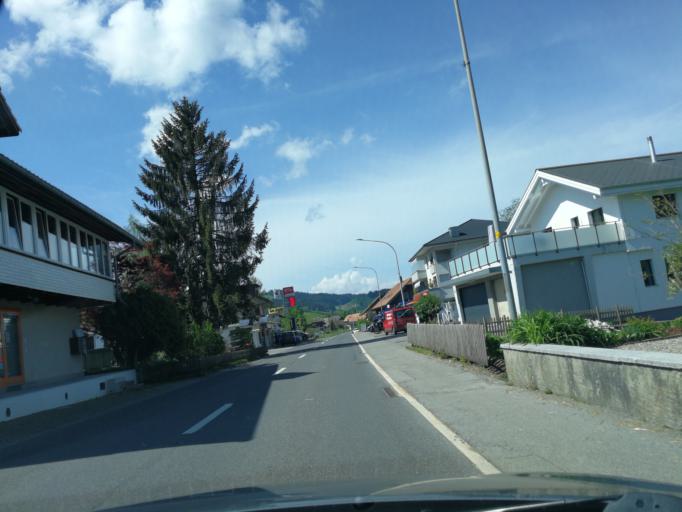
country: CH
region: Bern
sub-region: Bern-Mittelland District
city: Linden
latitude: 46.8463
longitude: 7.6768
